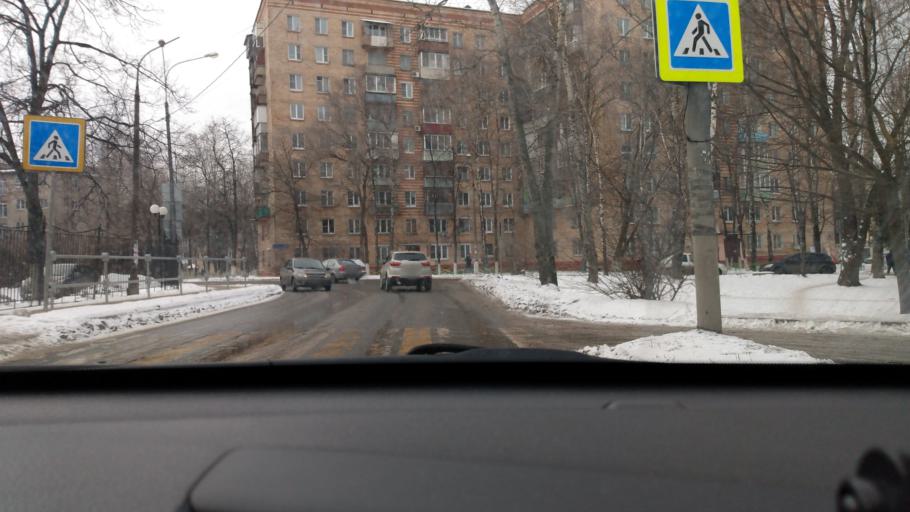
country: RU
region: Moskovskaya
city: Zheleznodorozhnyy
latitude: 55.7495
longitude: 37.9792
